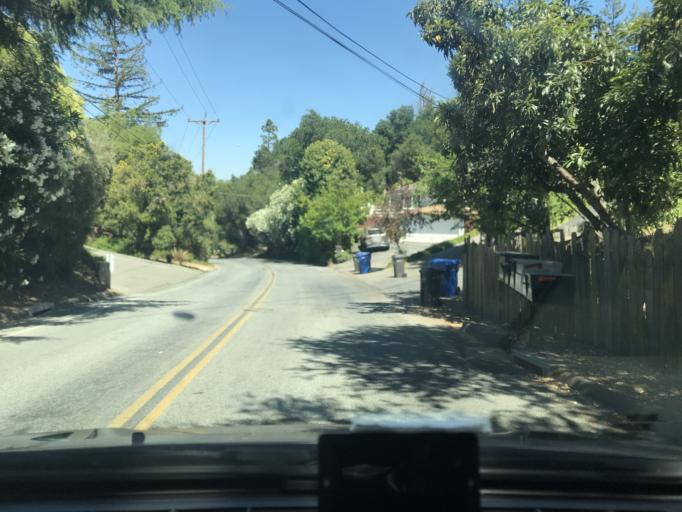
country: US
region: California
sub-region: Santa Clara County
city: Monte Sereno
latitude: 37.2305
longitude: -121.9939
